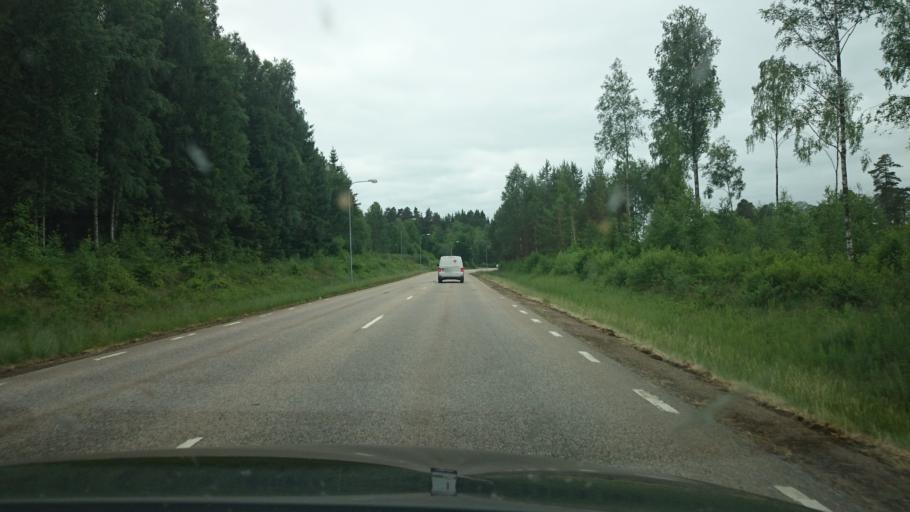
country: SE
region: Halland
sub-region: Hylte Kommun
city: Hyltebruk
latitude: 56.9902
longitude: 13.2277
